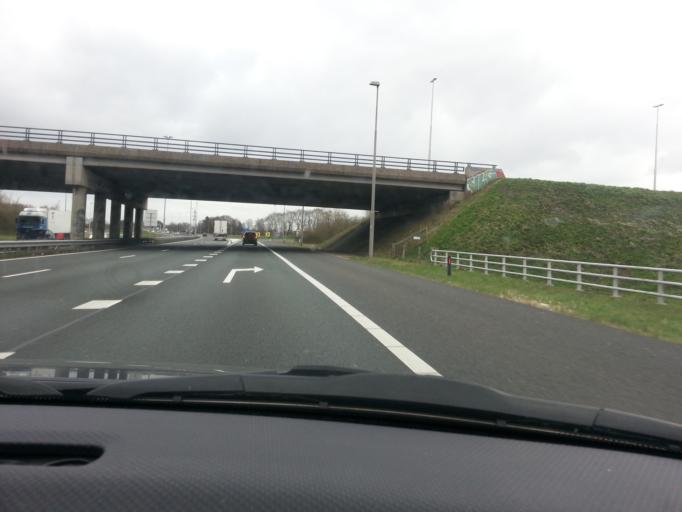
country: NL
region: North Brabant
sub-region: Gemeente Tilburg
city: Tilburg
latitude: 51.5612
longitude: 5.1356
